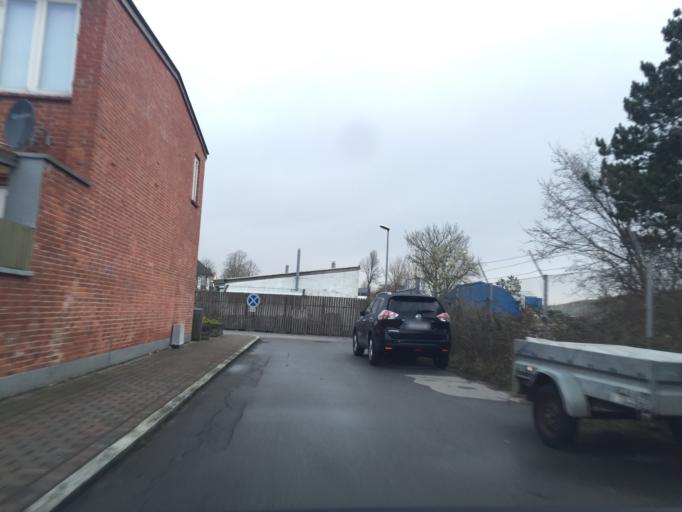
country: DK
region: Capital Region
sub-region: Tarnby Kommune
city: Tarnby
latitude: 55.6226
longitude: 12.6269
